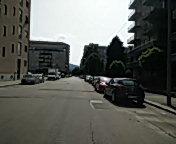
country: IT
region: Piedmont
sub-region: Provincia di Torino
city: Lesna
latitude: 45.0339
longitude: 7.6506
